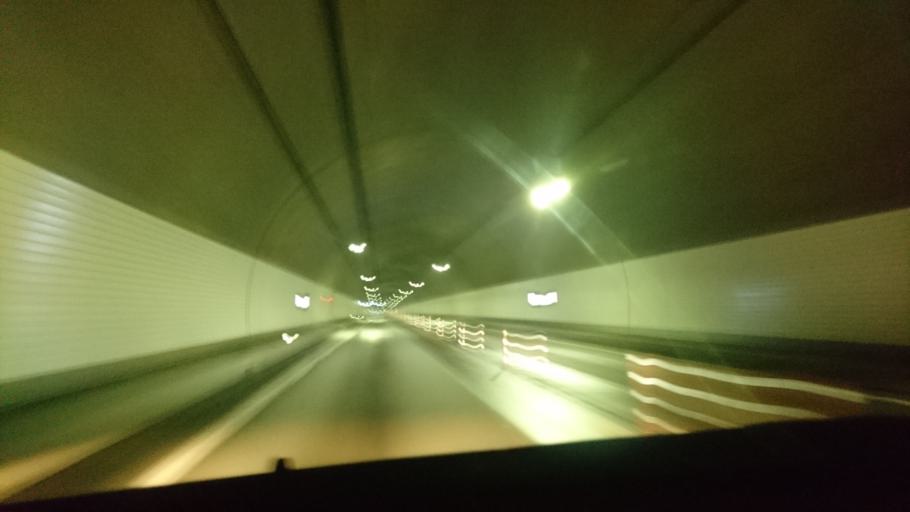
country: JP
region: Iwate
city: Miyako
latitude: 39.9281
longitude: 141.8762
